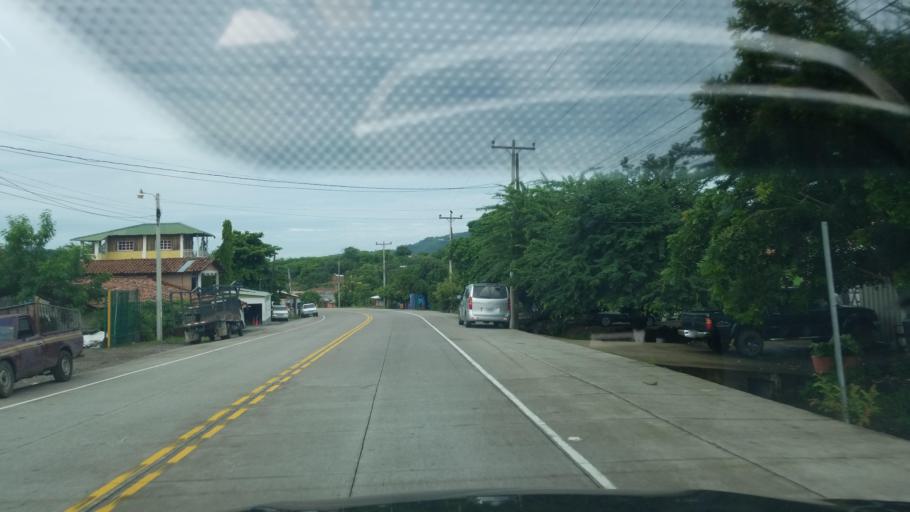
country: HN
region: Choluteca
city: Pespire
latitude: 13.6676
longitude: -87.3599
